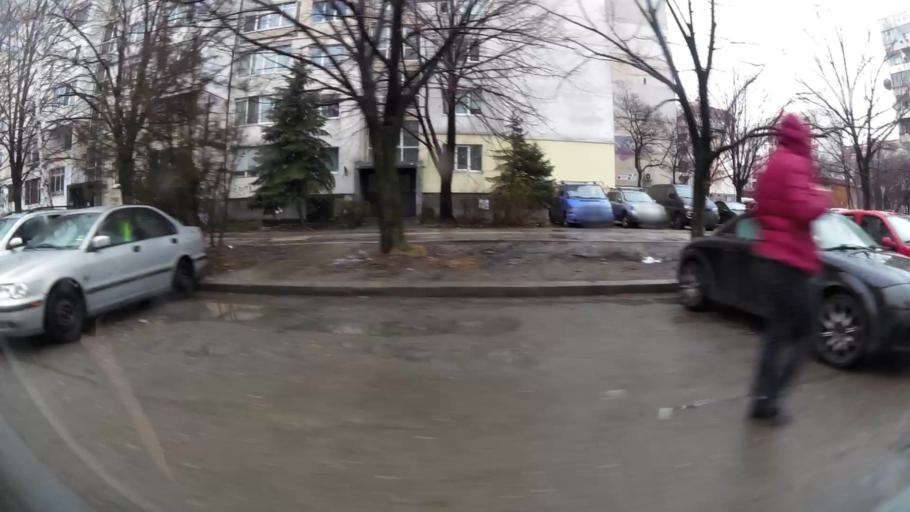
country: BG
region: Sofia-Capital
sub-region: Stolichna Obshtina
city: Sofia
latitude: 42.6402
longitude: 23.3762
